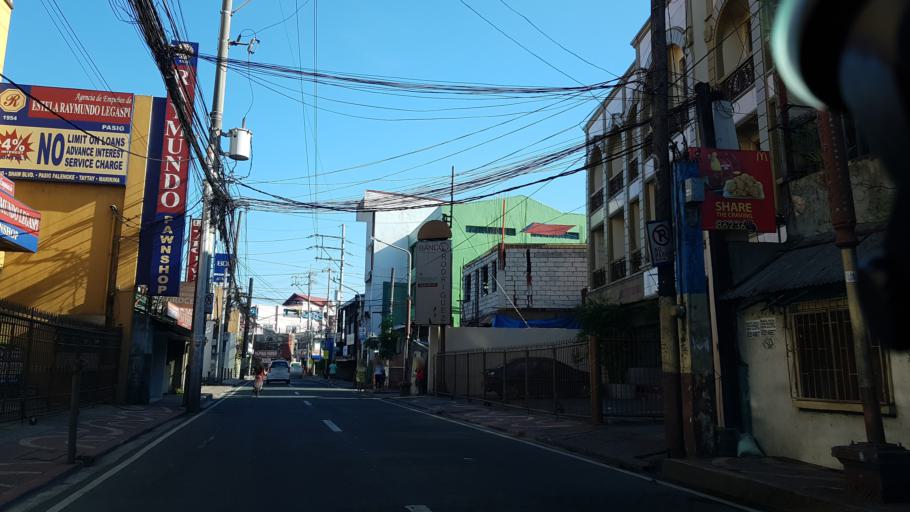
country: PH
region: Calabarzon
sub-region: Province of Rizal
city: Pateros
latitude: 14.5635
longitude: 121.0766
